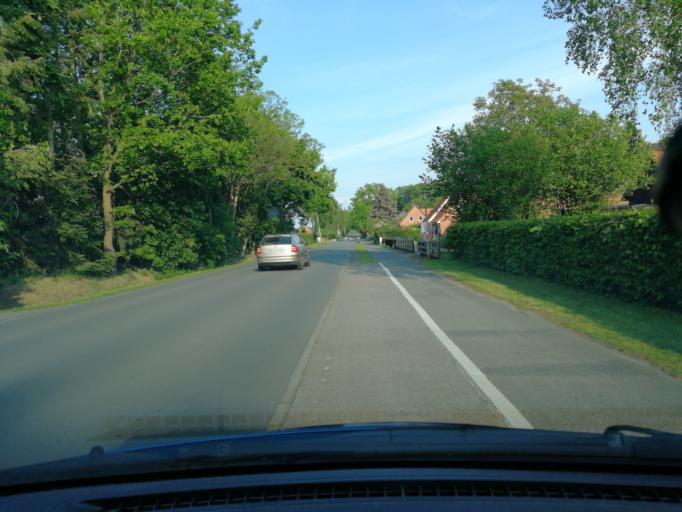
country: DE
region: Lower Saxony
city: Scharnebeck
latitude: 53.2935
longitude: 10.5144
